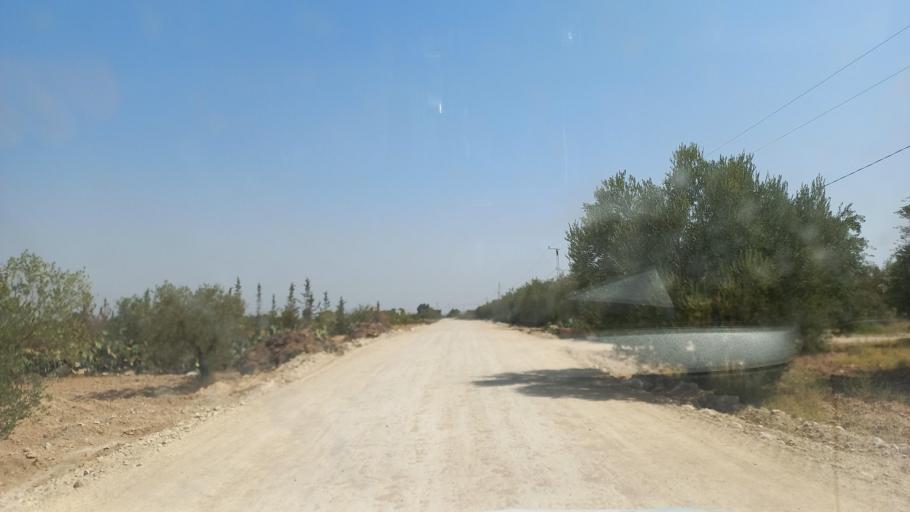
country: TN
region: Al Qasrayn
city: Kasserine
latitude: 35.2576
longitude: 9.0132
